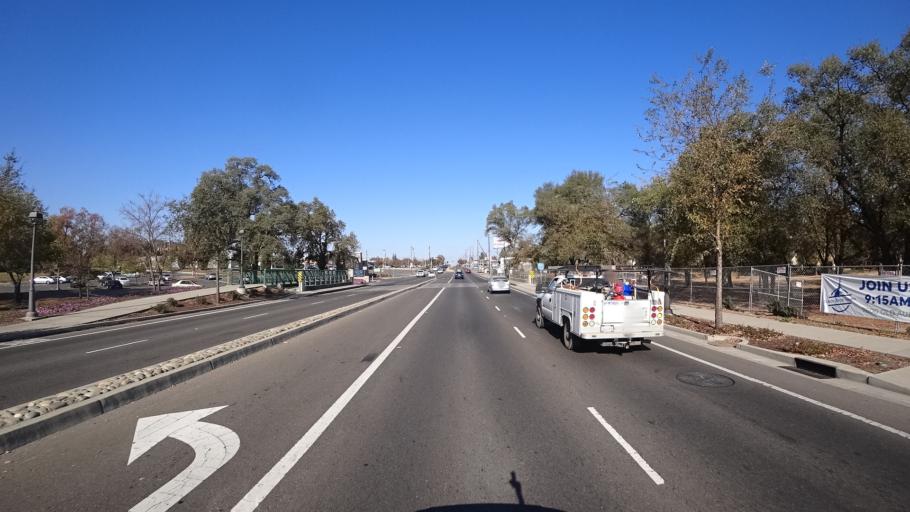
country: US
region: California
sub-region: Sacramento County
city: Citrus Heights
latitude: 38.7083
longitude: -121.2904
